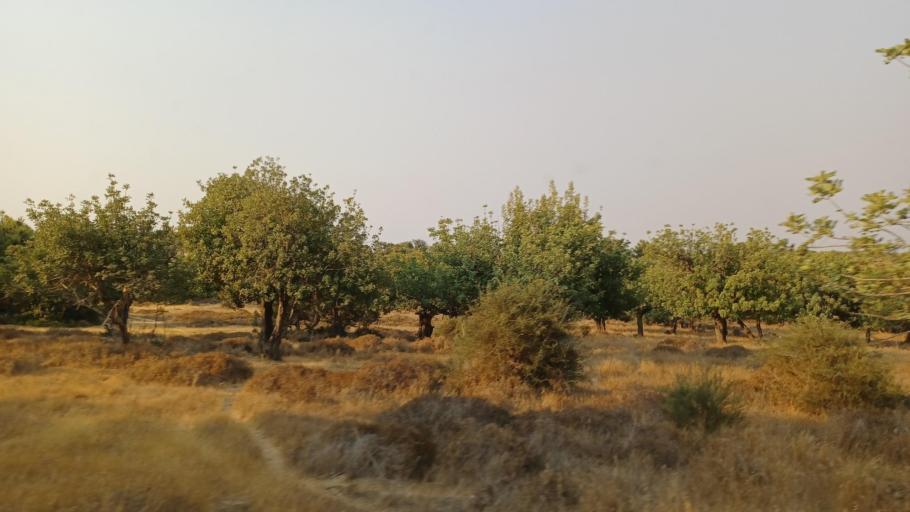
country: CY
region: Limassol
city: Pissouri
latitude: 34.6962
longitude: 32.6583
